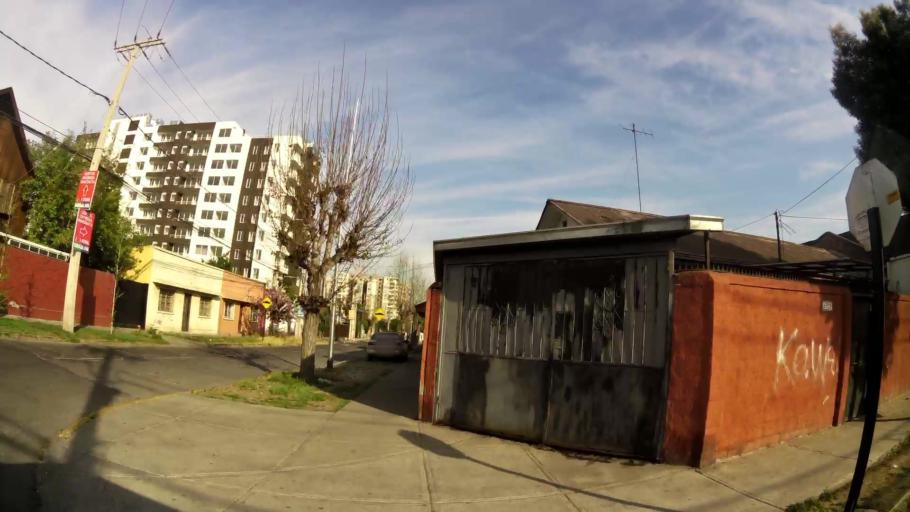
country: CL
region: Santiago Metropolitan
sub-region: Provincia de Santiago
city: Santiago
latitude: -33.5155
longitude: -70.6630
